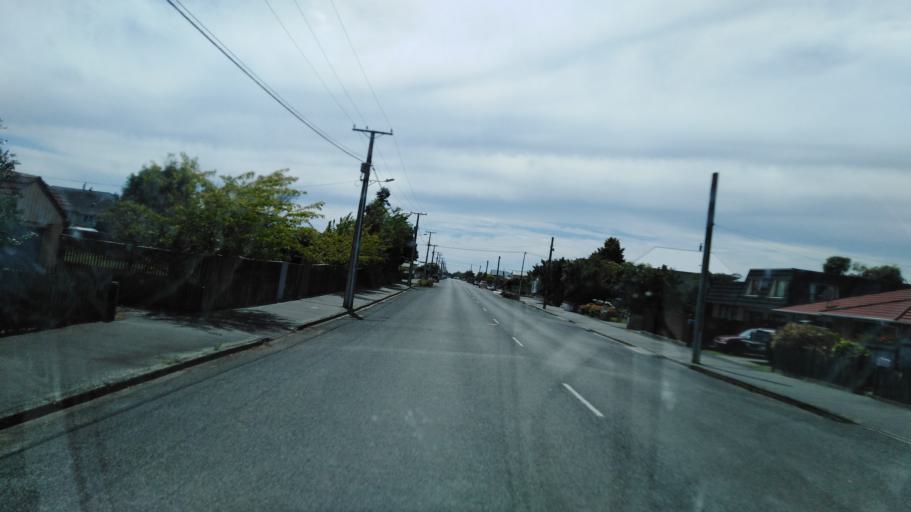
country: NZ
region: West Coast
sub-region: Buller District
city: Westport
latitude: -41.7505
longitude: 171.6049
